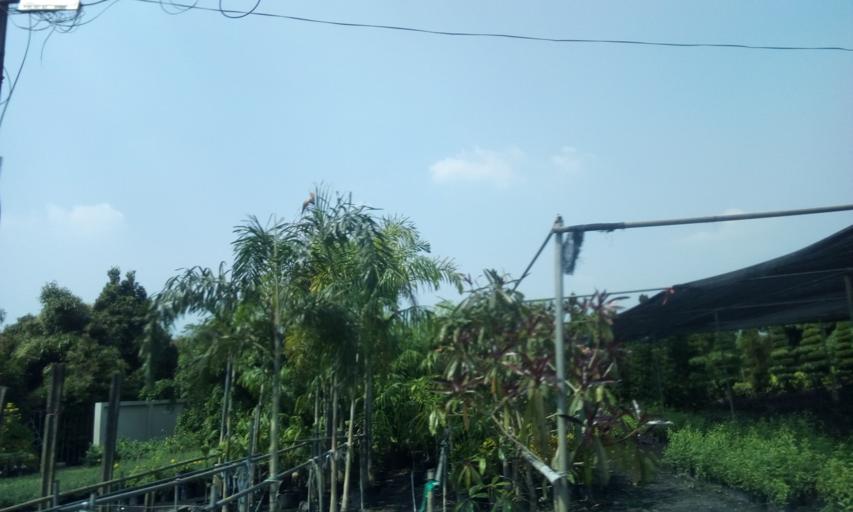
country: TH
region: Nakhon Nayok
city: Ongkharak
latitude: 14.1317
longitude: 100.9548
